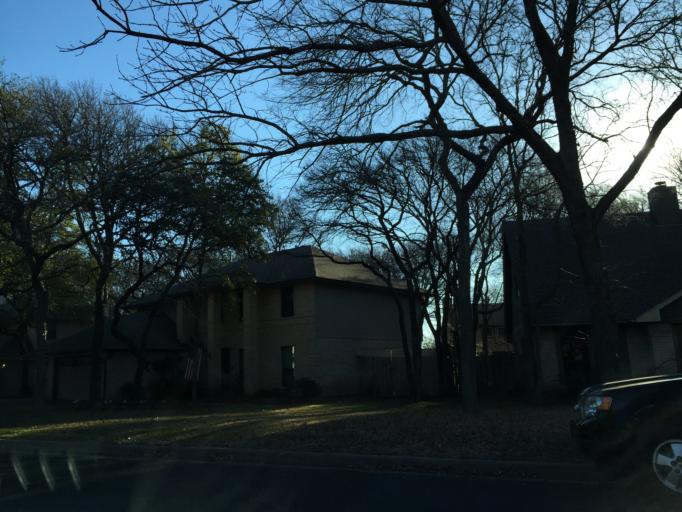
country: US
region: Texas
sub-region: Williamson County
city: Jollyville
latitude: 30.4430
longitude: -97.7667
